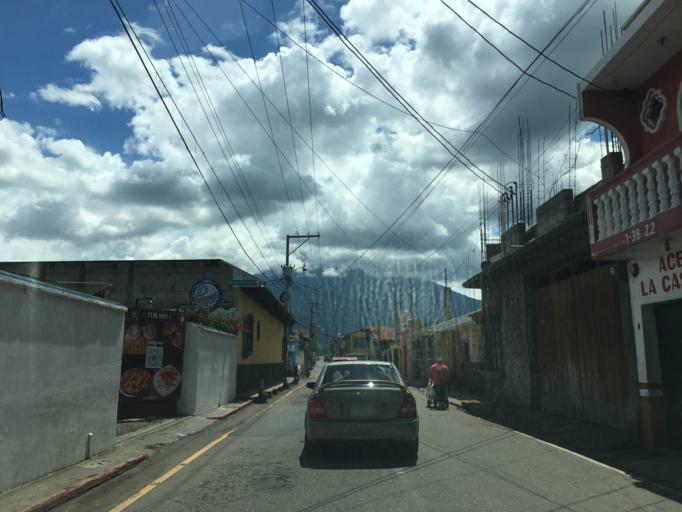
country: GT
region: Sacatepequez
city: Ciudad Vieja
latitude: 14.5259
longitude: -90.7654
